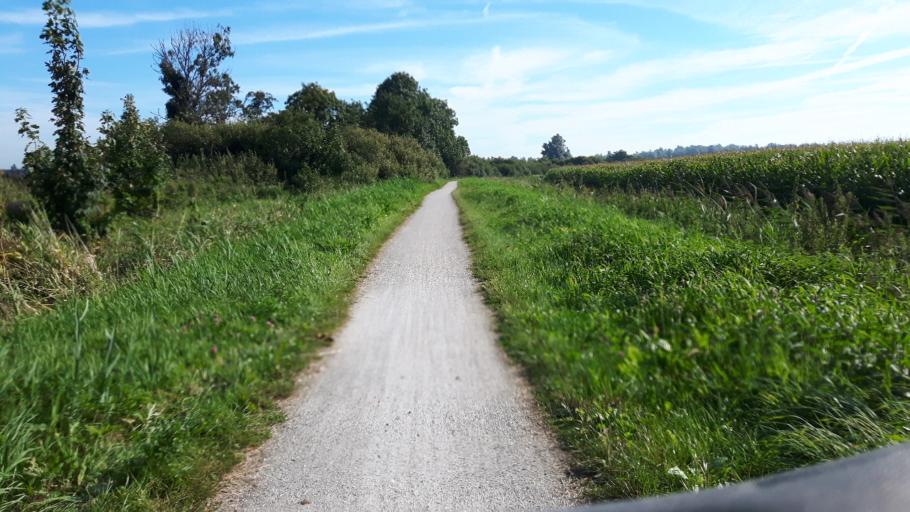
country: NL
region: Friesland
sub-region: Gemeente Skarsterlan
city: Sint Nicolaasga
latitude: 52.9679
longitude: 5.7510
